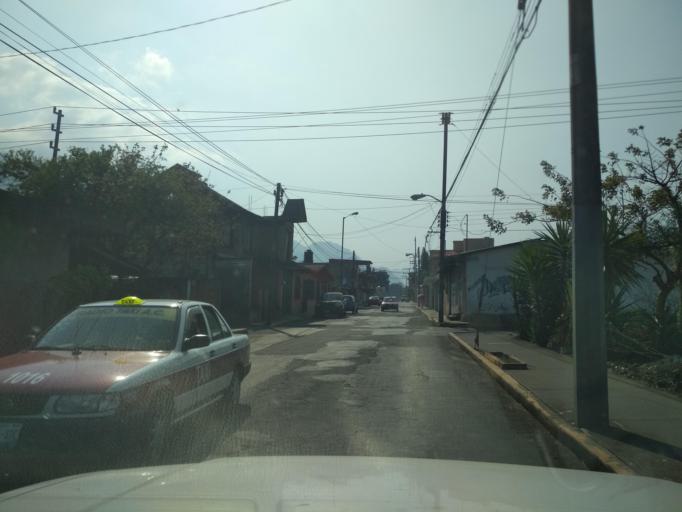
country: MX
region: Veracruz
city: Jalapilla
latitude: 18.8361
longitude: -97.0853
